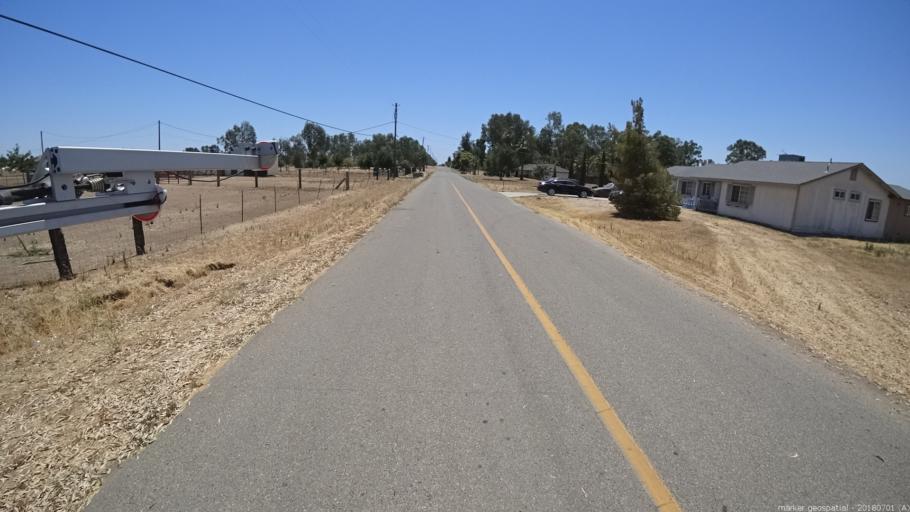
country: US
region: California
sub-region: Madera County
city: Madera Acres
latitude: 37.0466
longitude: -119.9867
